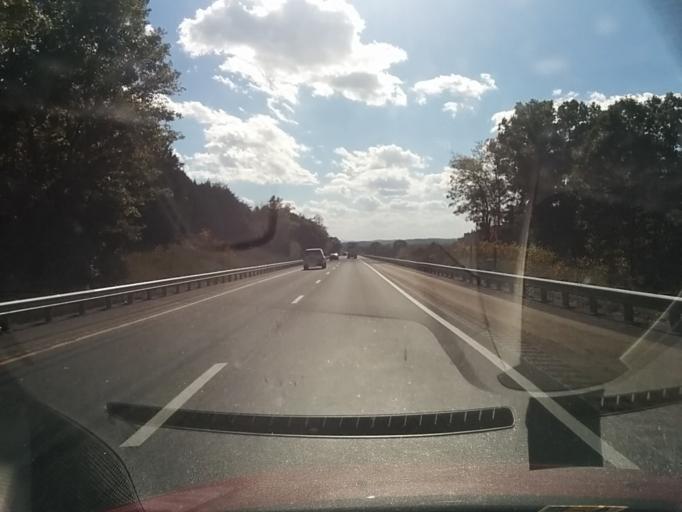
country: US
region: Virginia
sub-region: Rockbridge County
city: East Lexington
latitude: 37.8212
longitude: -79.3798
